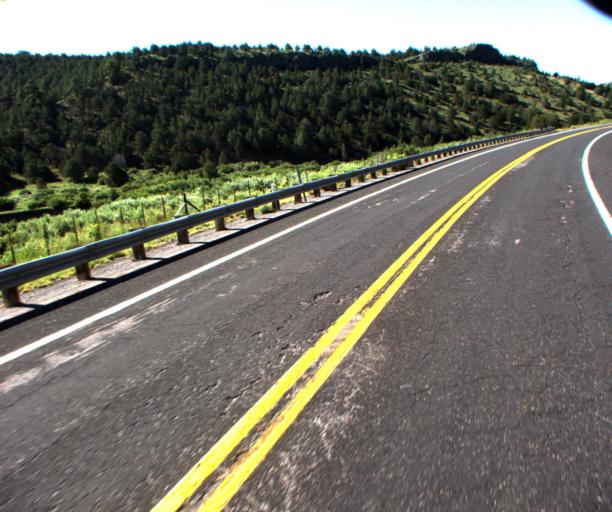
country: US
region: Arizona
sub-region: Apache County
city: Eagar
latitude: 34.0777
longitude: -109.1982
